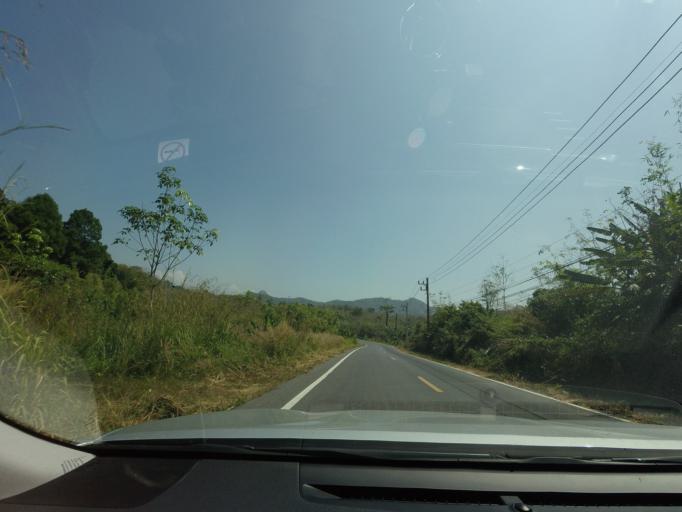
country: TH
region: Phangnga
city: Takua Thung
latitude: 8.2532
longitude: 98.4093
